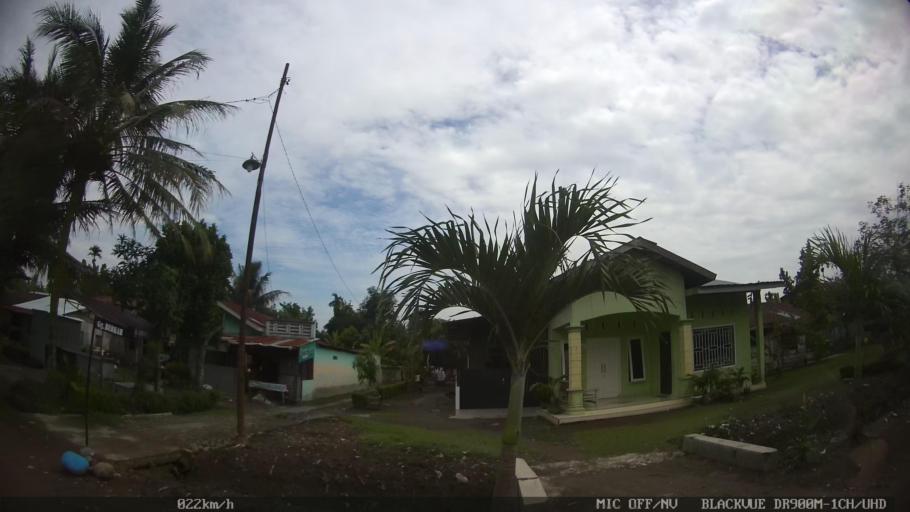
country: ID
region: North Sumatra
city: Sunggal
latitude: 3.6620
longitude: 98.5935
